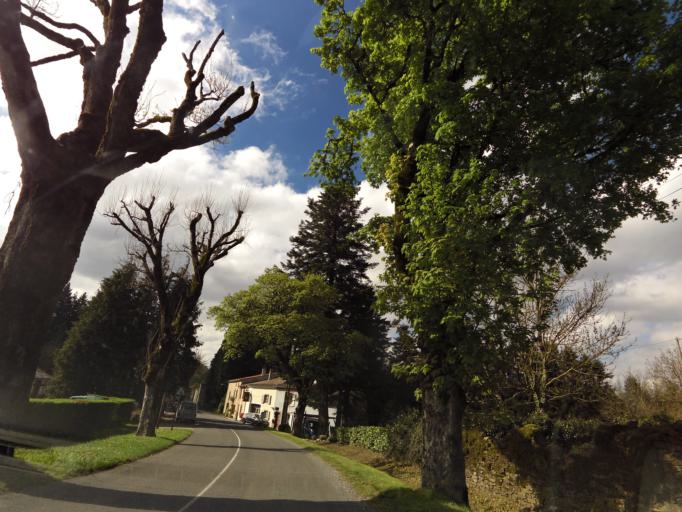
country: FR
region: Midi-Pyrenees
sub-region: Departement du Tarn
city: Soreze
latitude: 43.4089
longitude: 2.0813
